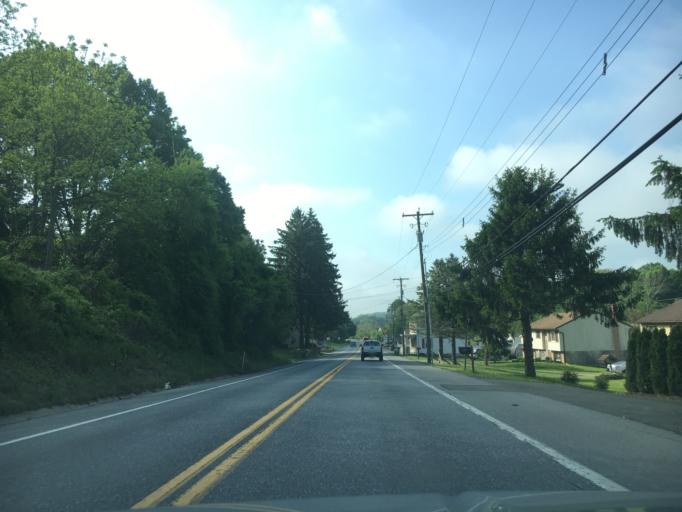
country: US
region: Pennsylvania
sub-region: Berks County
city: Boyertown
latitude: 40.3439
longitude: -75.6600
